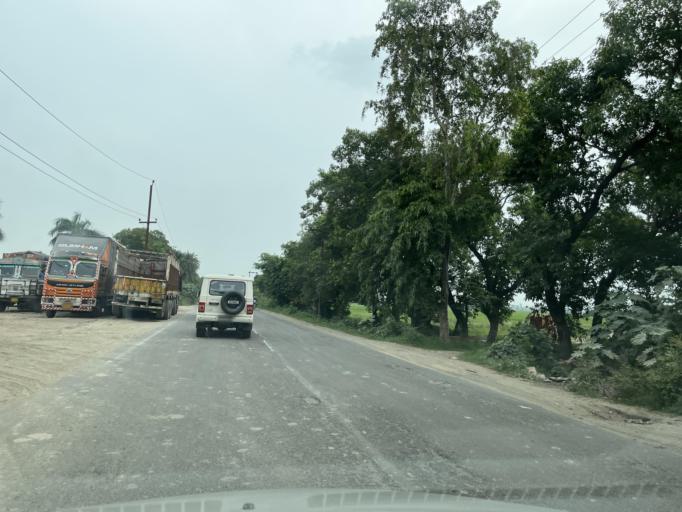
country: IN
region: Uttar Pradesh
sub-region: Rampur
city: Bilaspur
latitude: 29.0268
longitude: 79.2685
